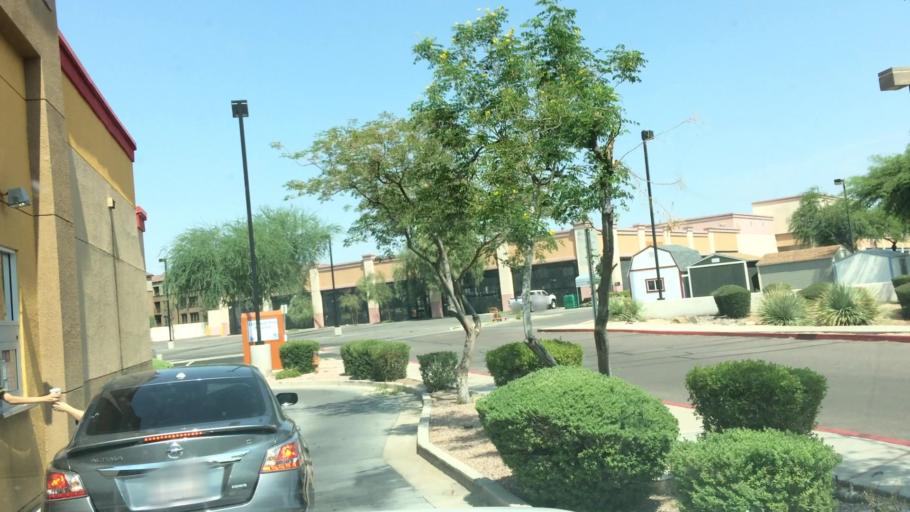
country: US
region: Arizona
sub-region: Maricopa County
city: Paradise Valley
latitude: 33.6238
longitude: -111.8960
